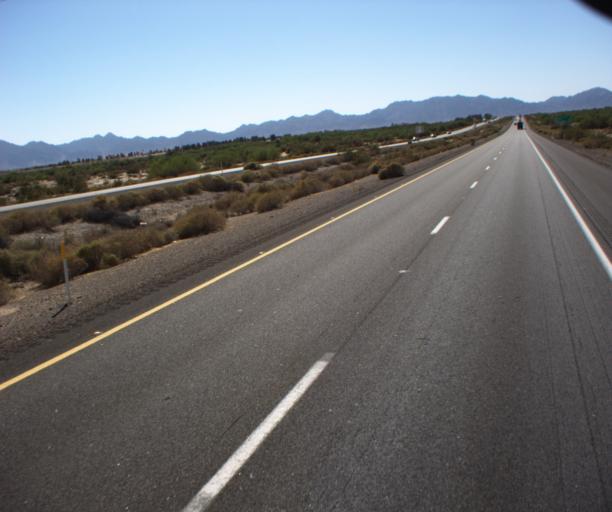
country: US
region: Arizona
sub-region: Yuma County
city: Wellton
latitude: 32.6584
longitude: -114.1577
